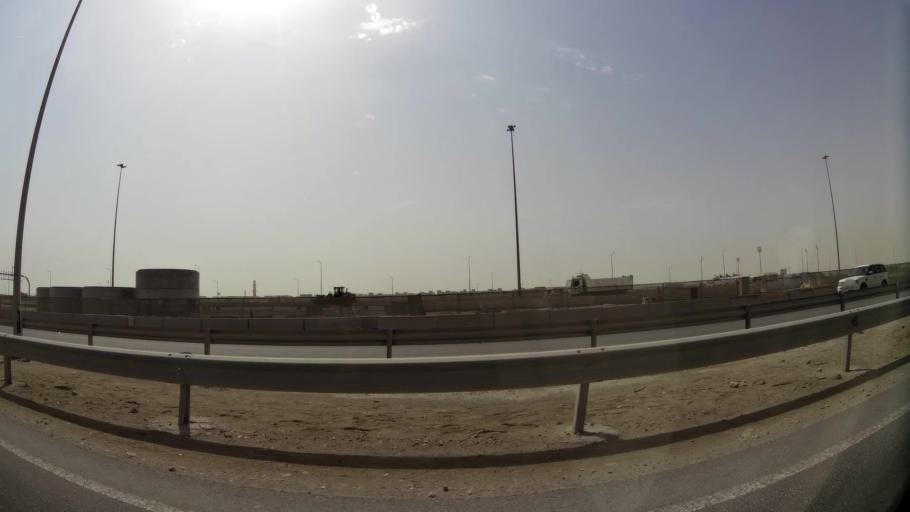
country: QA
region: Al Wakrah
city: Al Wukayr
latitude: 25.1962
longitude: 51.4622
